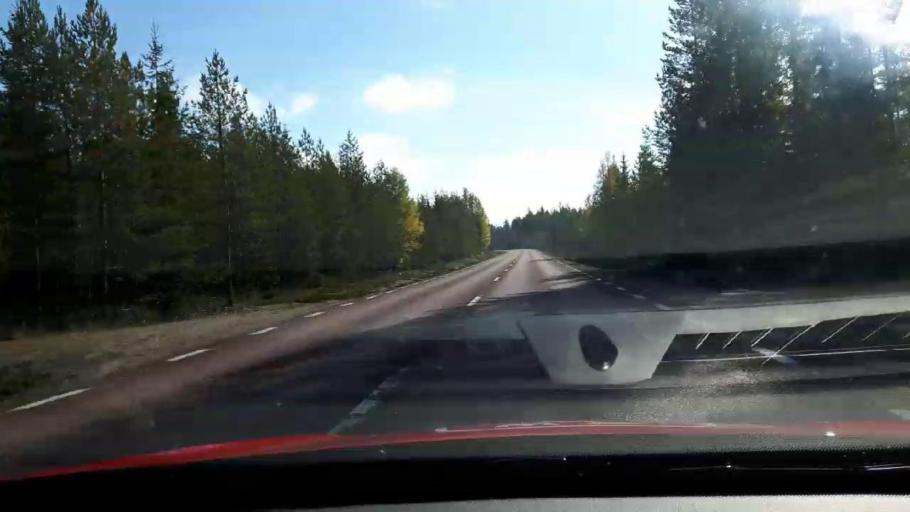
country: SE
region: Gaevleborg
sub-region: Ljusdals Kommun
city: Farila
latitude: 61.9221
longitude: 15.6047
